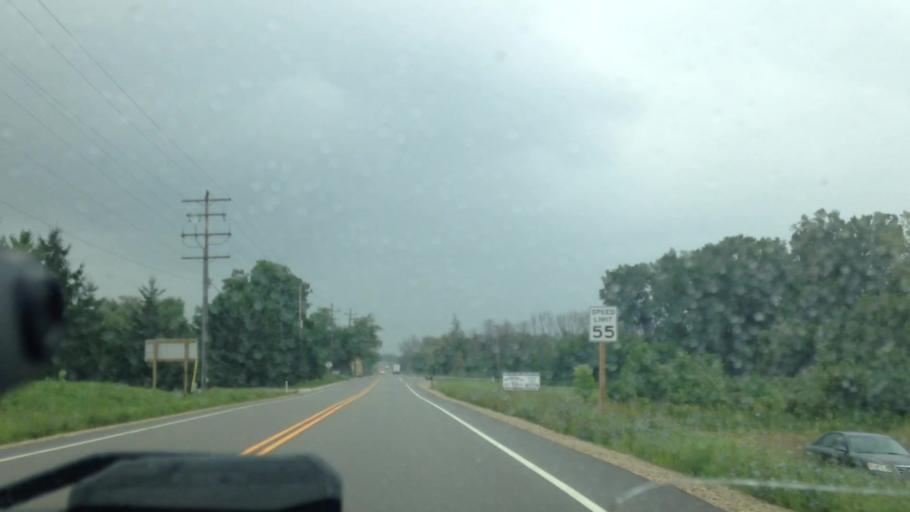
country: US
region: Wisconsin
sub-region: Washington County
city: Richfield
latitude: 43.2938
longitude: -88.2200
